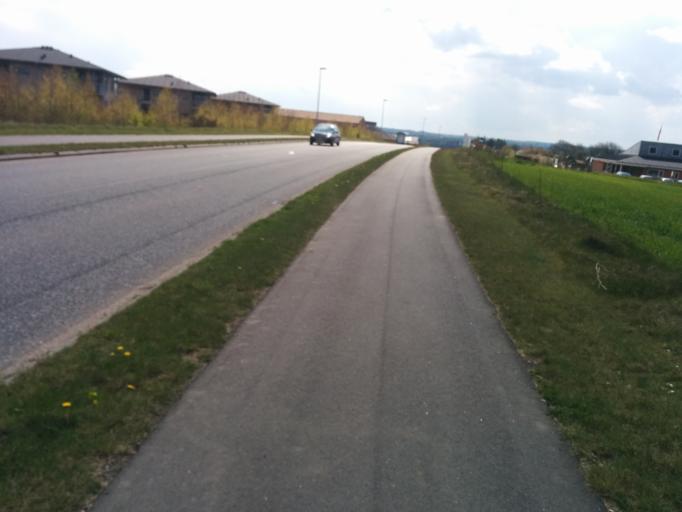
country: DK
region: Central Jutland
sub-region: Viborg Kommune
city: Viborg
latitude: 56.4452
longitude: 9.3617
